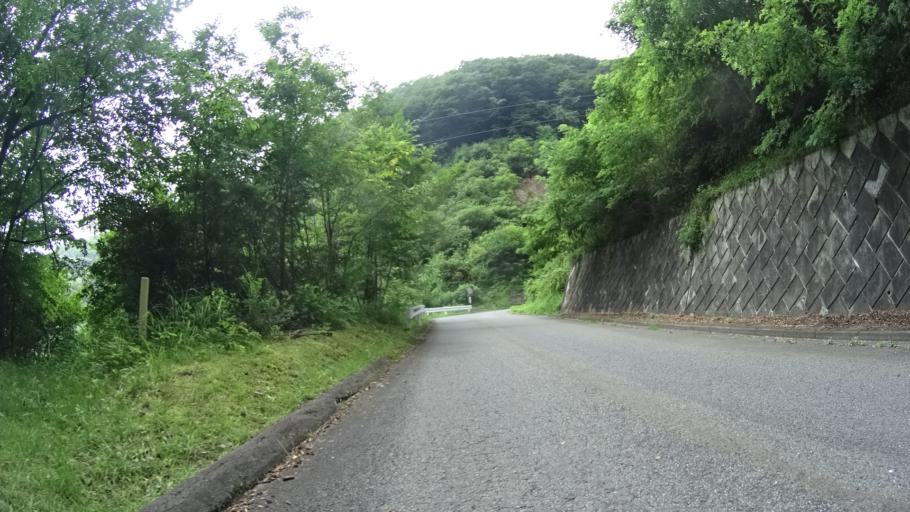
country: JP
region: Nagano
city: Saku
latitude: 36.0907
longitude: 138.6855
